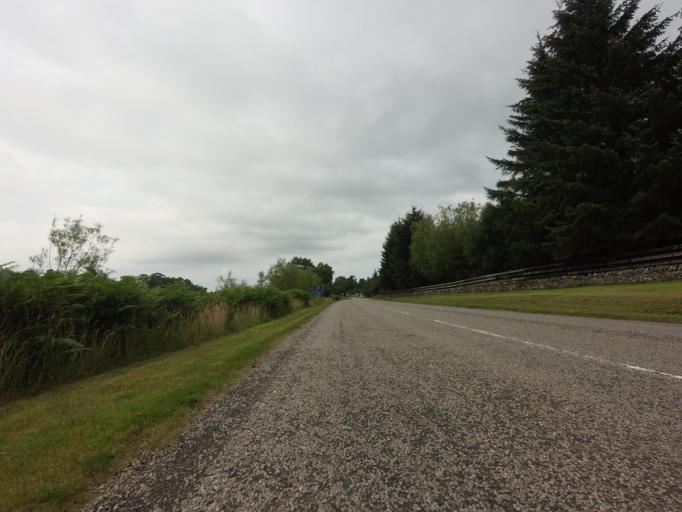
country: GB
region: Scotland
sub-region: Highland
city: Evanton
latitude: 57.9214
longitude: -4.3988
